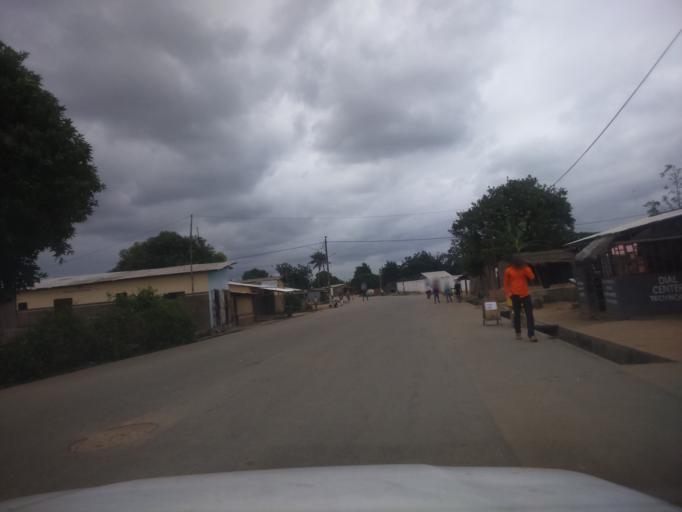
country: CI
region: Sud-Comoe
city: Adiake
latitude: 5.2880
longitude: -3.3064
